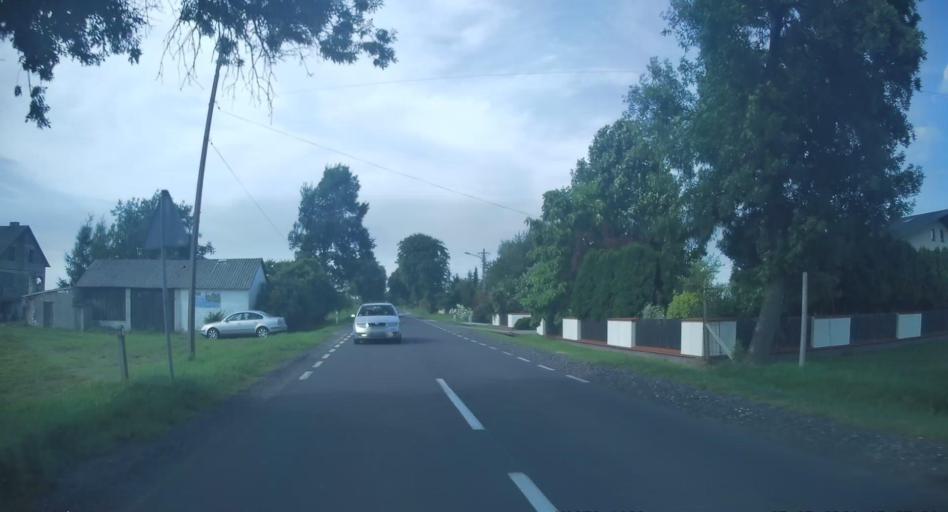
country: PL
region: Lodz Voivodeship
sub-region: Powiat tomaszowski
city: Rzeczyca
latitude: 51.6073
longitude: 20.2935
